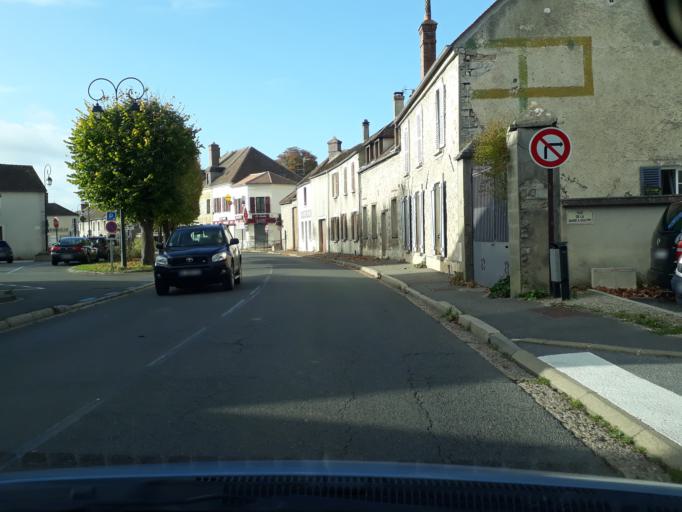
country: FR
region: Ile-de-France
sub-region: Departement de Seine-et-Marne
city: Acheres-la-Foret
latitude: 48.3435
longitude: 2.6020
